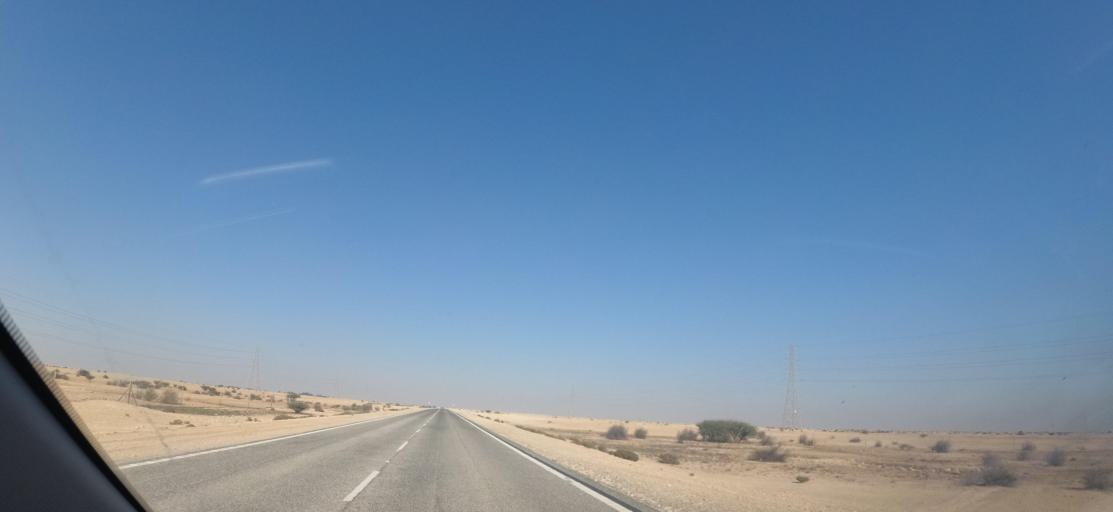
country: QA
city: Al Jumayliyah
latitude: 25.6537
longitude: 51.1137
